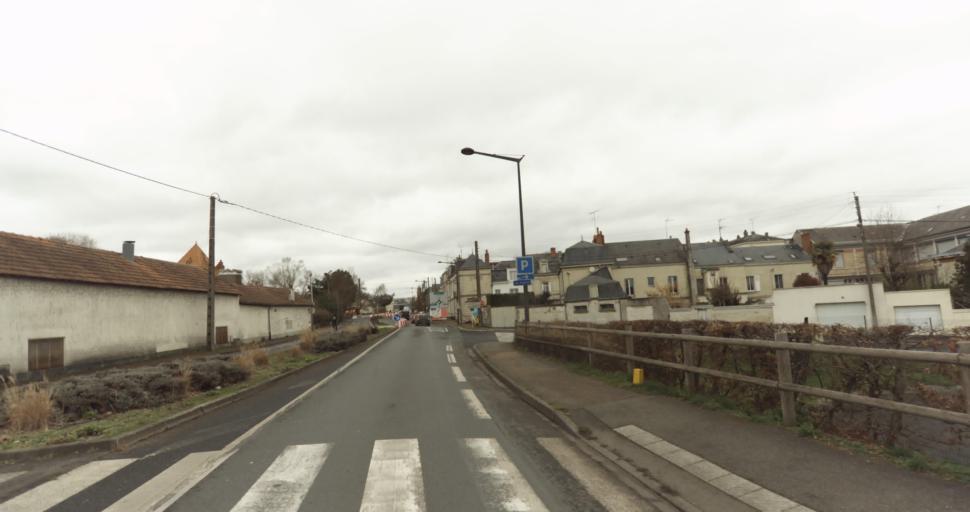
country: FR
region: Pays de la Loire
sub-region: Departement de Maine-et-Loire
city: Saumur
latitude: 47.2527
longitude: -0.0835
